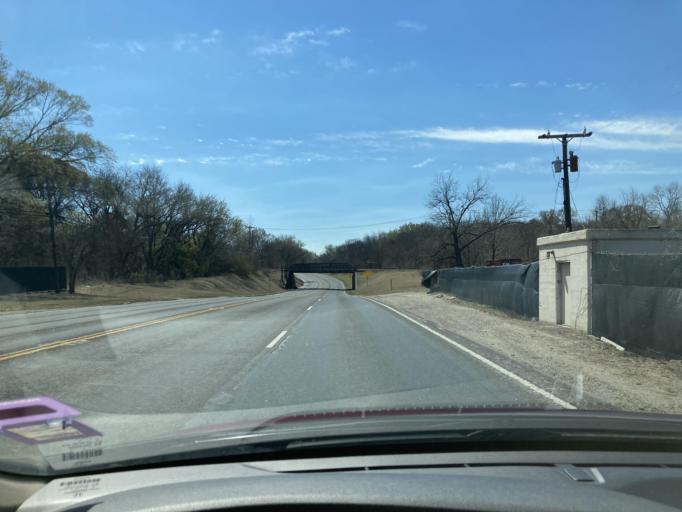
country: US
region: Texas
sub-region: Navarro County
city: Corsicana
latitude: 32.1035
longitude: -96.4637
